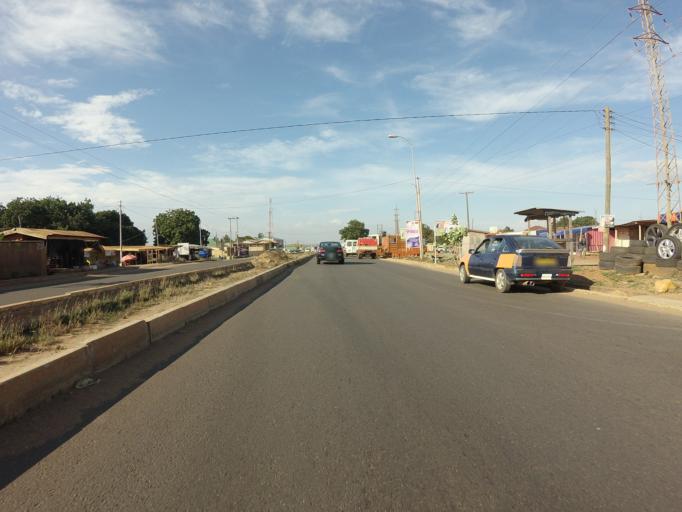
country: GH
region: Greater Accra
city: Nungua
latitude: 5.6410
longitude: -0.0611
